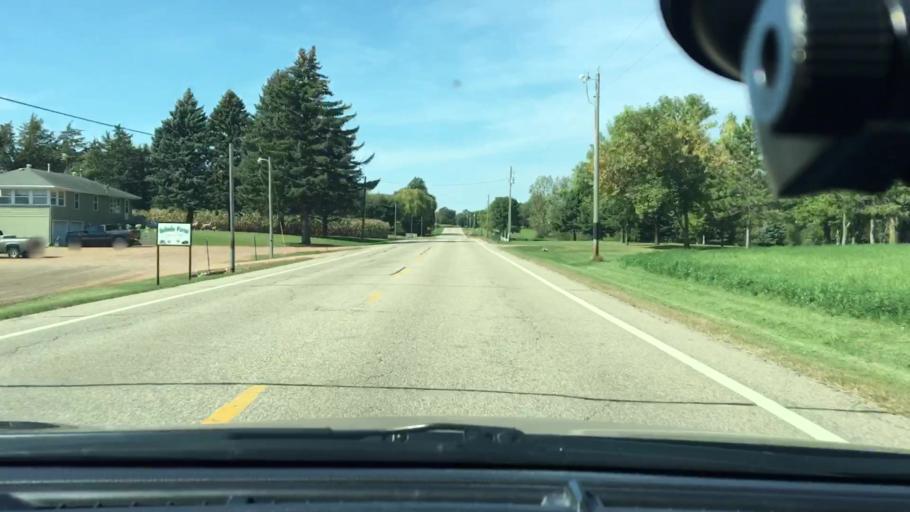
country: US
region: Minnesota
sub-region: Hennepin County
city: Corcoran
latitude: 45.1126
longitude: -93.5753
